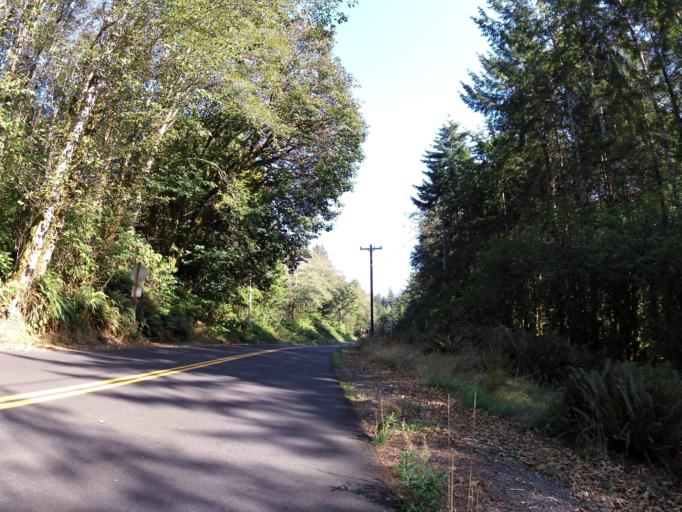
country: US
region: Oregon
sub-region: Lincoln County
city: Rose Lodge
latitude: 45.0845
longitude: -123.9523
